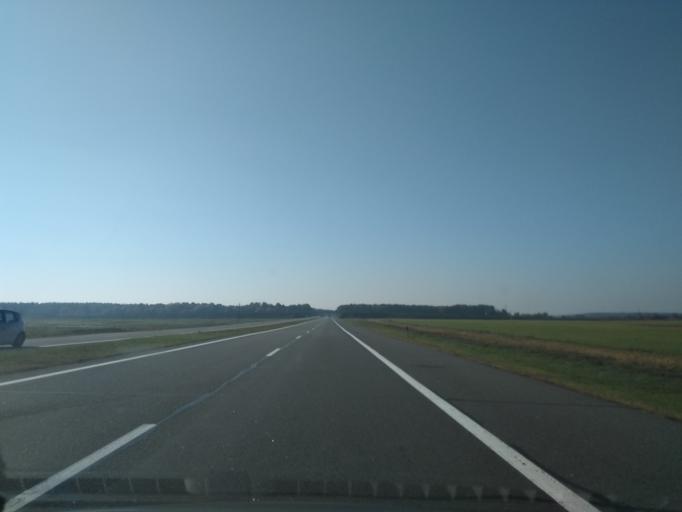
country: BY
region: Brest
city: Ivatsevichy
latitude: 52.7274
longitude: 25.4449
